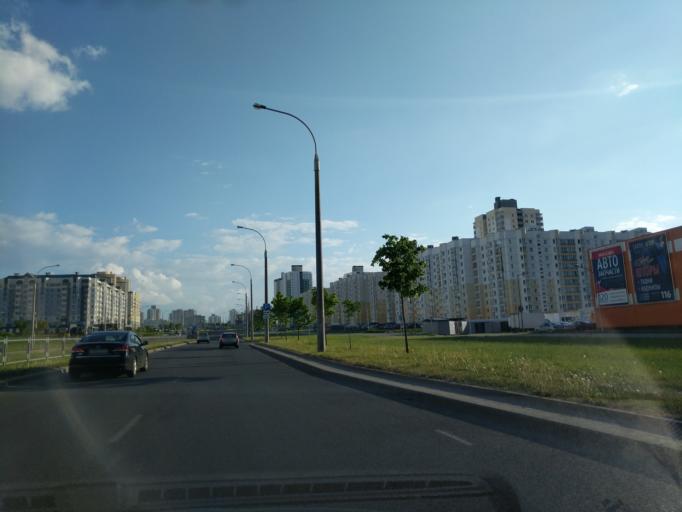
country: BY
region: Minsk
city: Zhdanovichy
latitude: 53.9263
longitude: 27.4417
